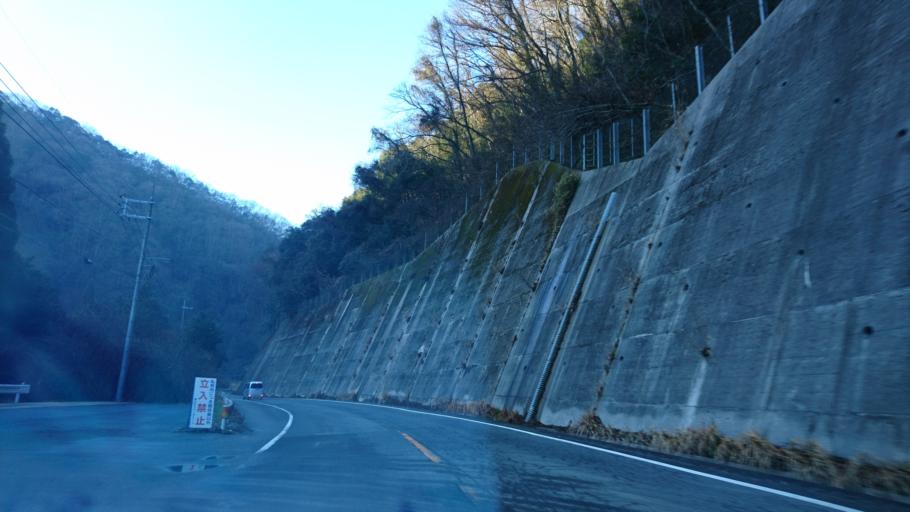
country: JP
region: Okayama
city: Takahashi
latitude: 34.8197
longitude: 133.6526
